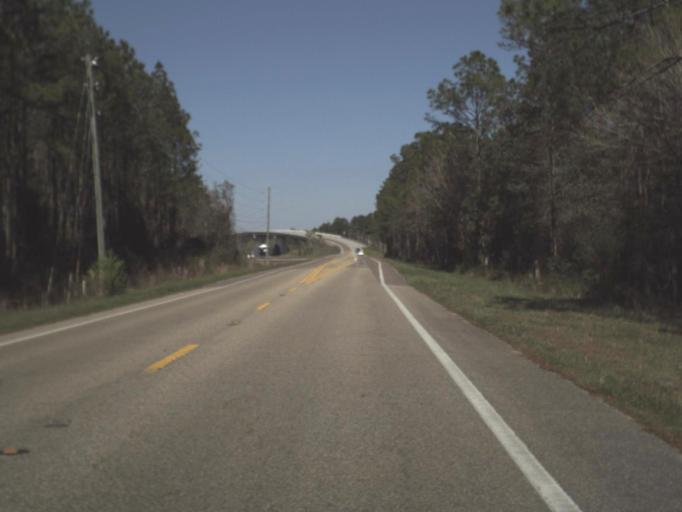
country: US
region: Florida
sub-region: Gulf County
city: Port Saint Joe
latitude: 29.8746
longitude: -85.2278
